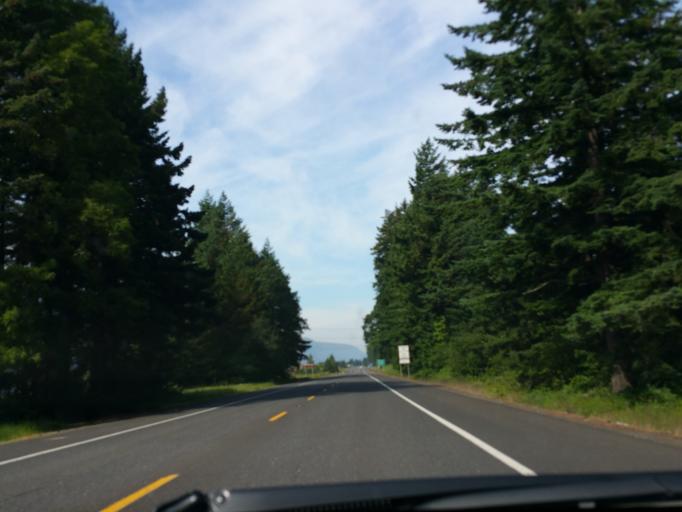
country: US
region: Oregon
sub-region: Hood River County
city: Cascade Locks
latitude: 45.6495
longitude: -121.9491
